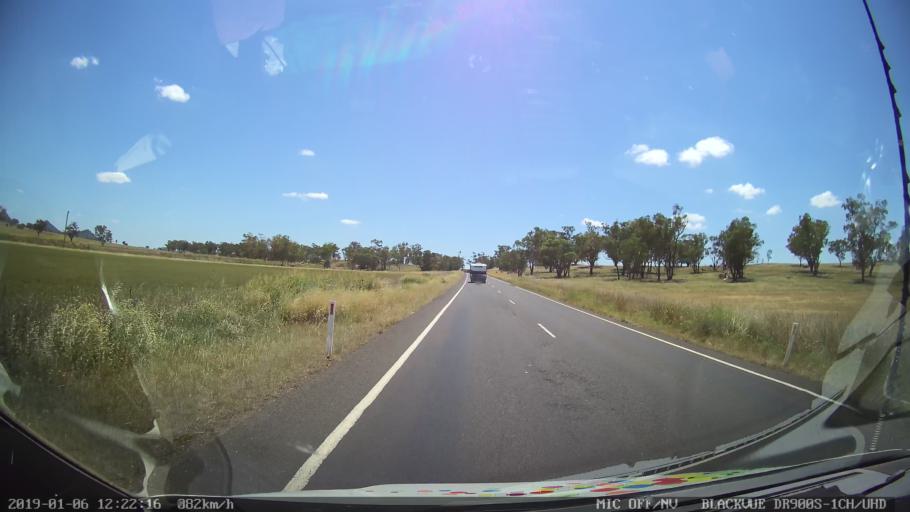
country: AU
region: New South Wales
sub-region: Tamworth Municipality
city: Phillip
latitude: -31.2637
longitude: 150.7868
